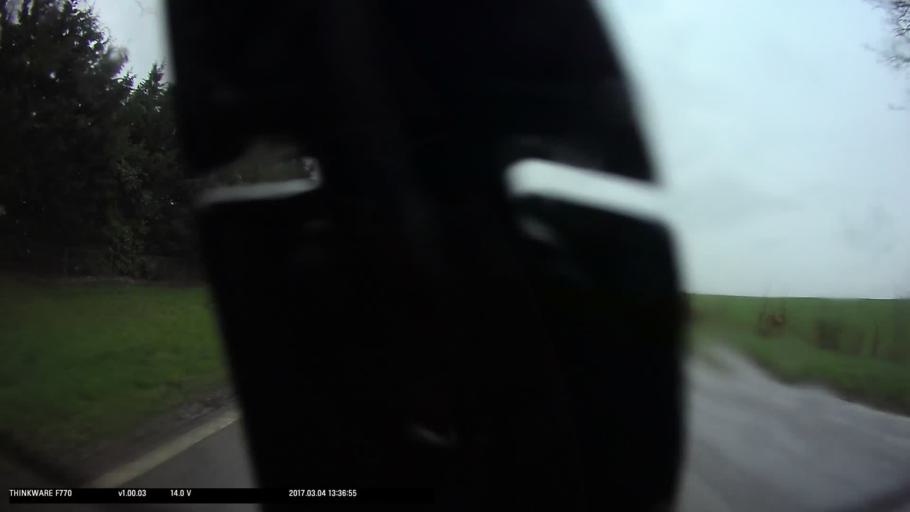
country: FR
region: Ile-de-France
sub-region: Departement du Val-d'Oise
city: Osny
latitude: 49.1049
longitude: 2.0372
